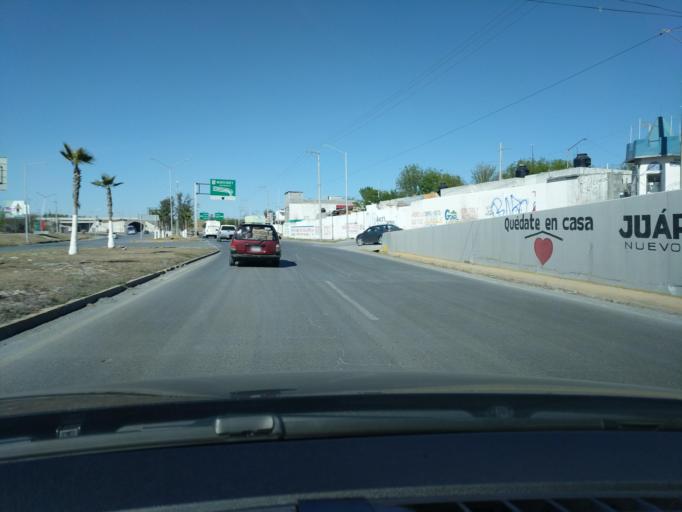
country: MX
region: Nuevo Leon
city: Juarez
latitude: 25.6567
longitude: -100.0796
